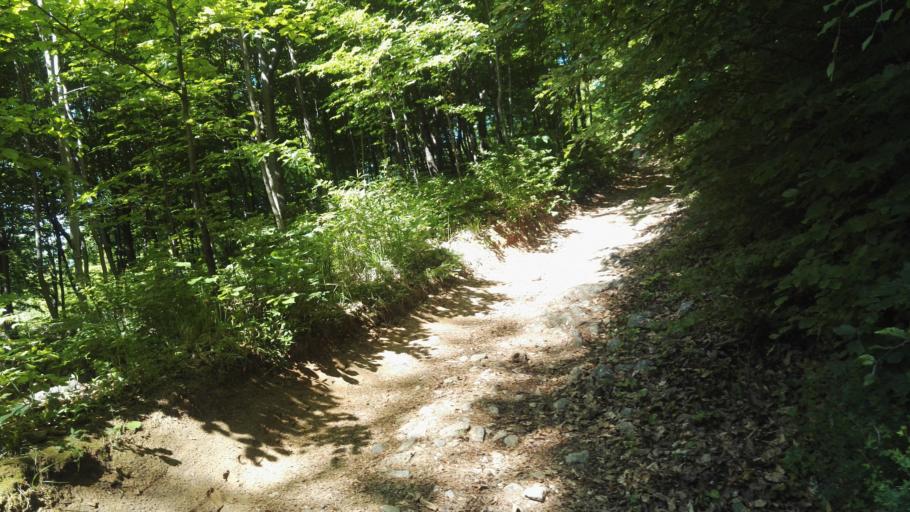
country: AT
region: Styria
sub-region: Politischer Bezirk Graz-Umgebung
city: Thal
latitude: 47.0728
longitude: 15.3709
